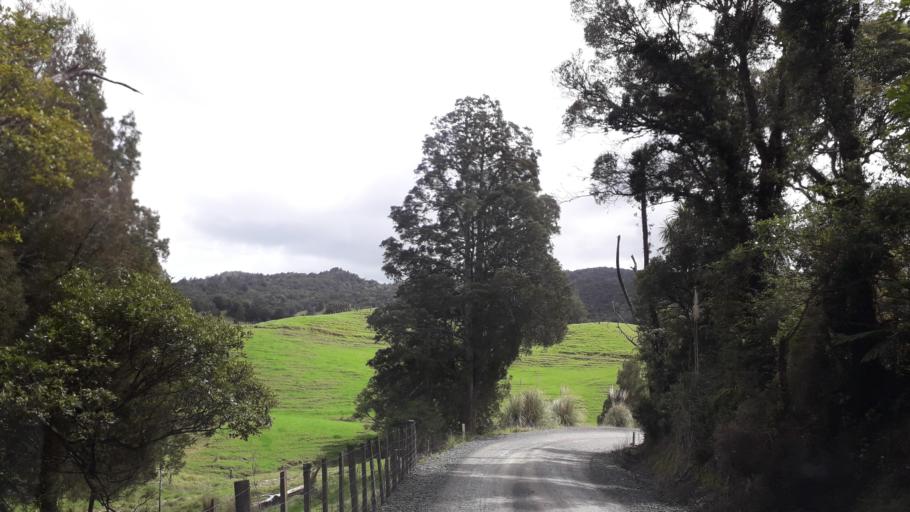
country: NZ
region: Northland
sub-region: Far North District
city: Kaitaia
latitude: -35.1898
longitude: 173.2916
